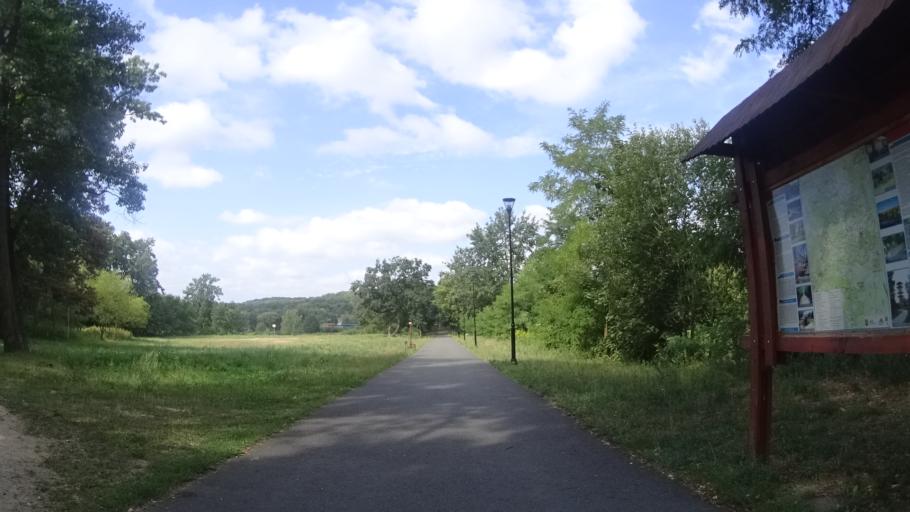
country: PL
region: Lubusz
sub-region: Powiat zarski
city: Leknica
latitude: 51.5365
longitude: 14.7363
